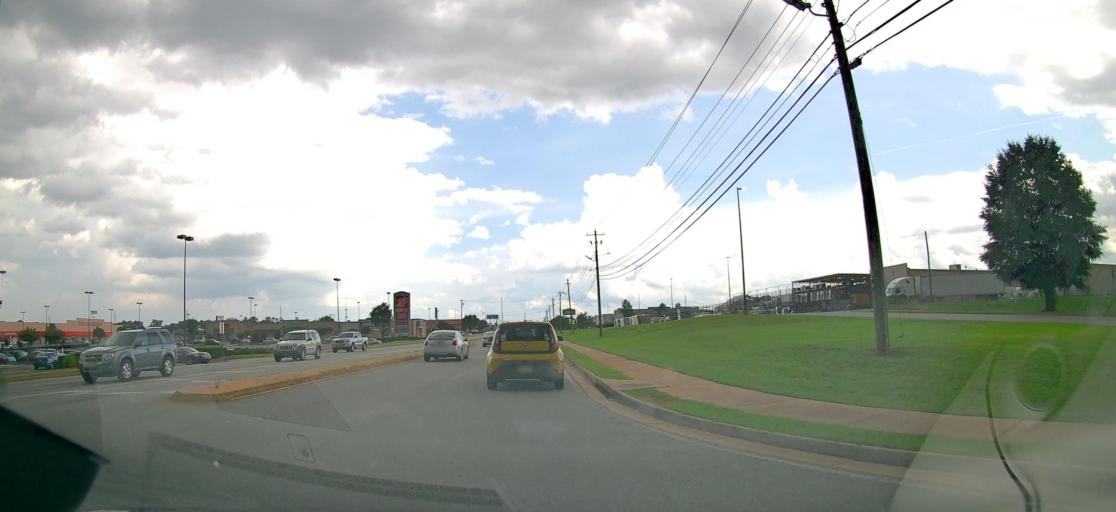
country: US
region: Georgia
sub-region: Houston County
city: Centerville
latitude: 32.6220
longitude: -83.6692
